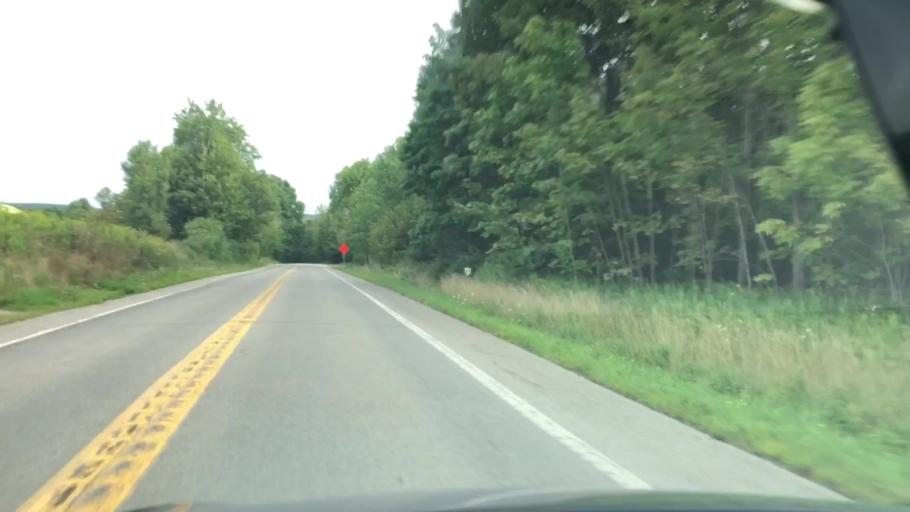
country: US
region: Pennsylvania
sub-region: Erie County
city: Union City
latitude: 41.8069
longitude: -79.7989
